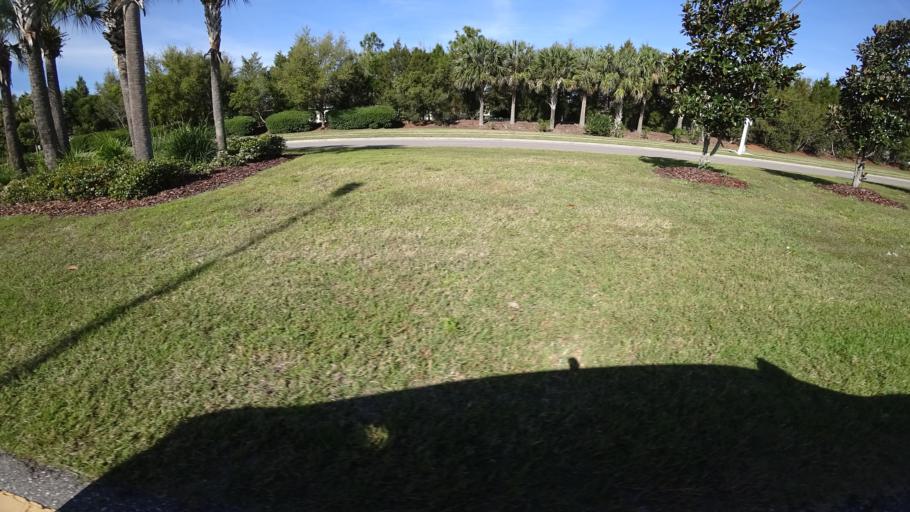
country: US
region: Florida
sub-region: Sarasota County
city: The Meadows
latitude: 27.4541
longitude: -82.4180
